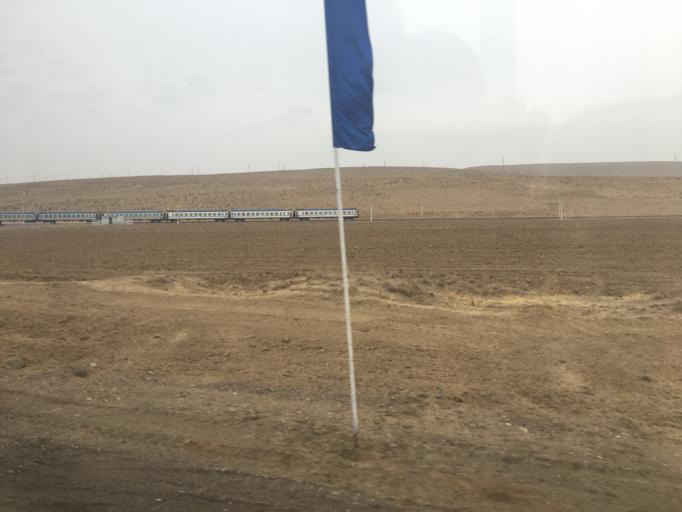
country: TM
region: Mary
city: Serhetabat
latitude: 35.4702
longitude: 62.4068
